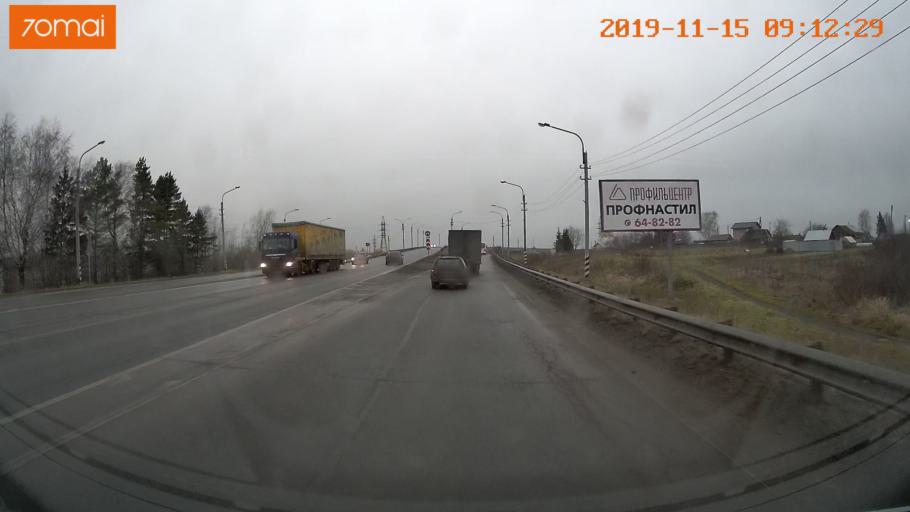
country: RU
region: Vologda
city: Tonshalovo
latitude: 59.2085
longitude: 37.9366
